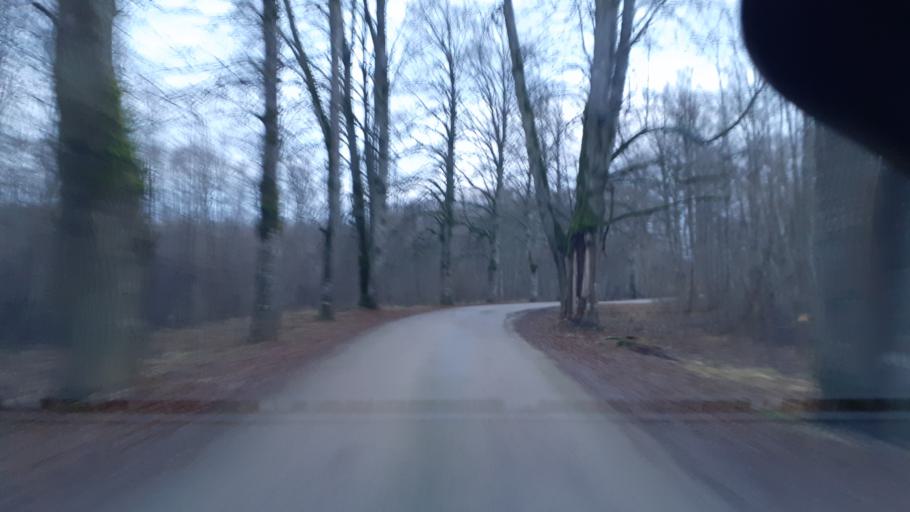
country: LV
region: Alsunga
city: Alsunga
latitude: 56.9008
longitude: 21.6994
